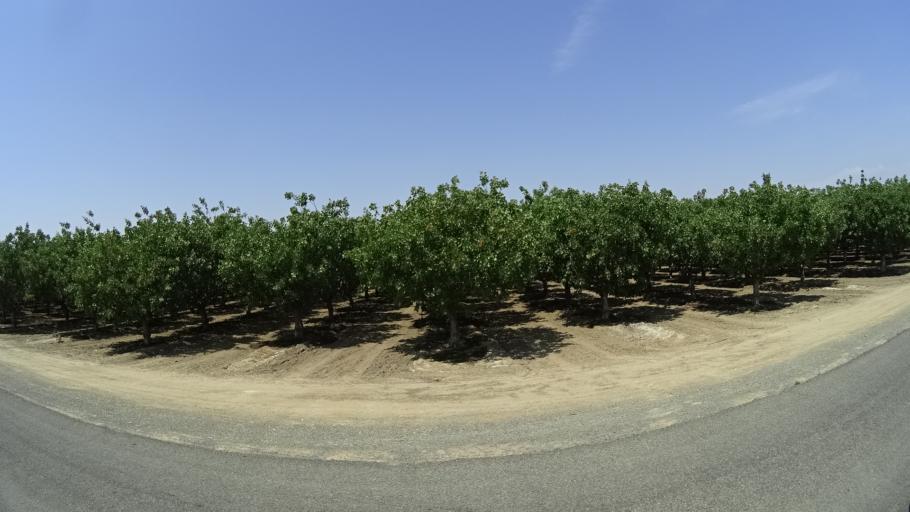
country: US
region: California
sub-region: Kings County
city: Lemoore
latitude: 36.3319
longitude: -119.7628
